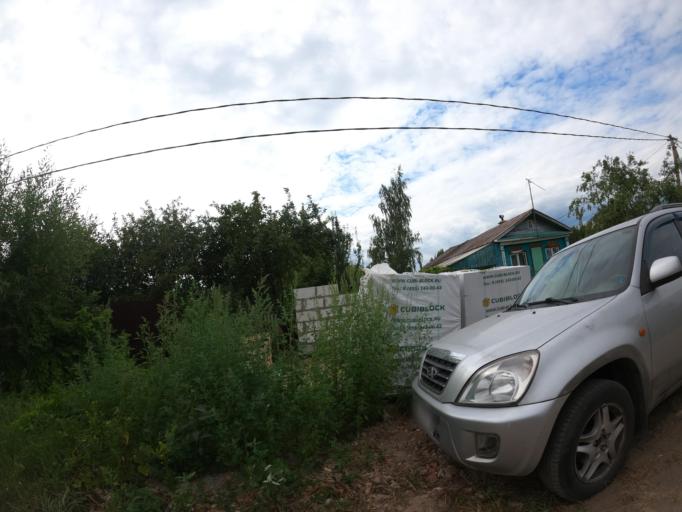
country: RU
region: Moskovskaya
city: Bronnitsy
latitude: 55.4836
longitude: 38.2552
